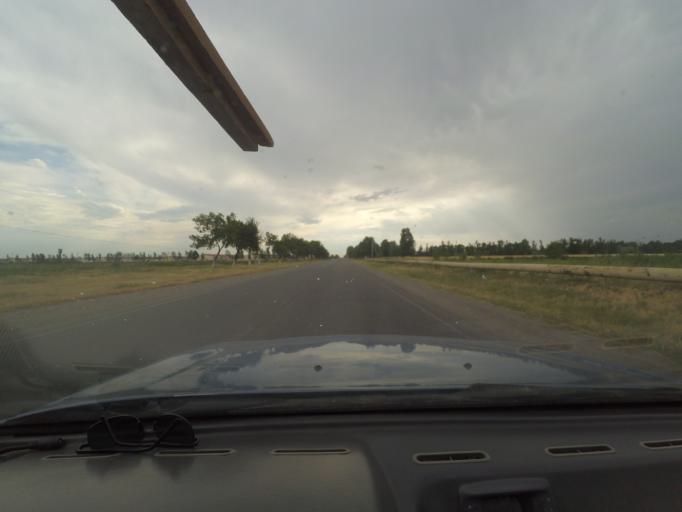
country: UZ
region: Sirdaryo
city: Guliston
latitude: 40.4924
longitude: 68.8309
